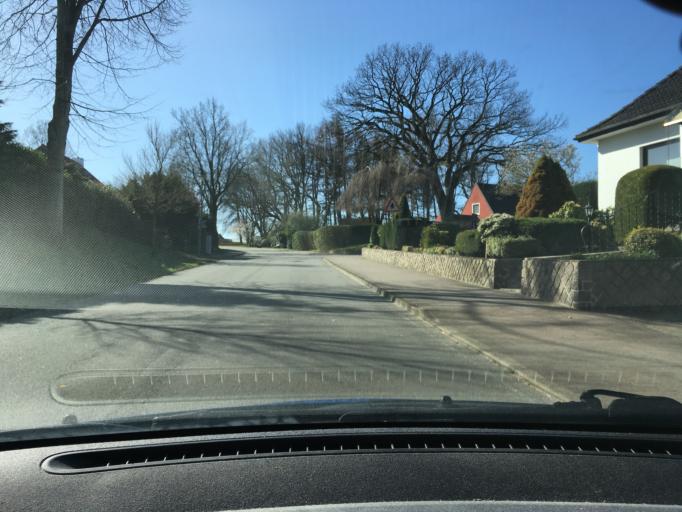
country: DE
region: Schleswig-Holstein
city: Fahrdorf
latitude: 54.5026
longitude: 9.5996
